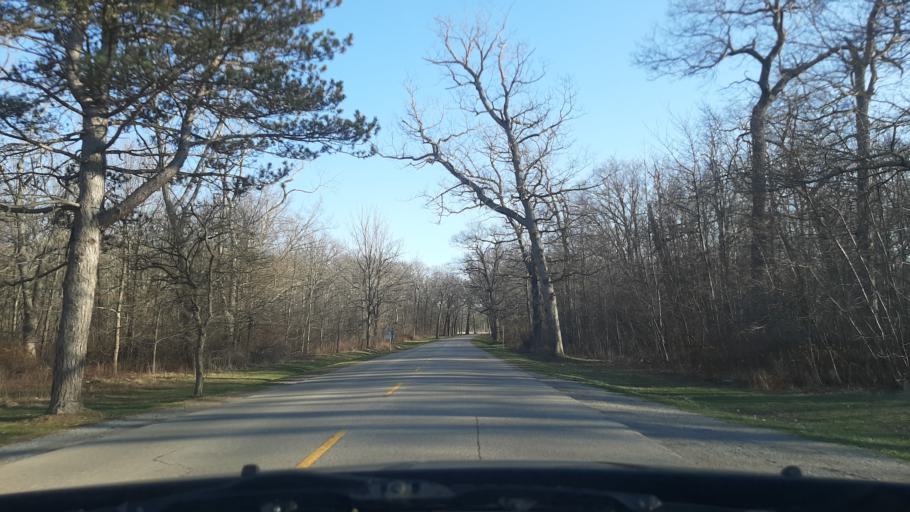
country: US
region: New York
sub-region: Niagara County
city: Youngstown
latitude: 43.2456
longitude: -79.0629
